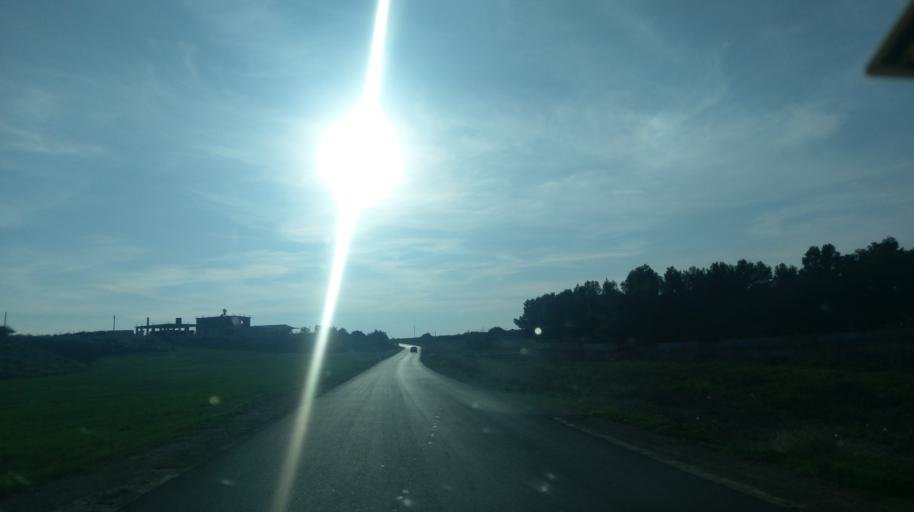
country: CY
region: Ammochostos
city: Acheritou
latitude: 35.1068
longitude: 33.8665
